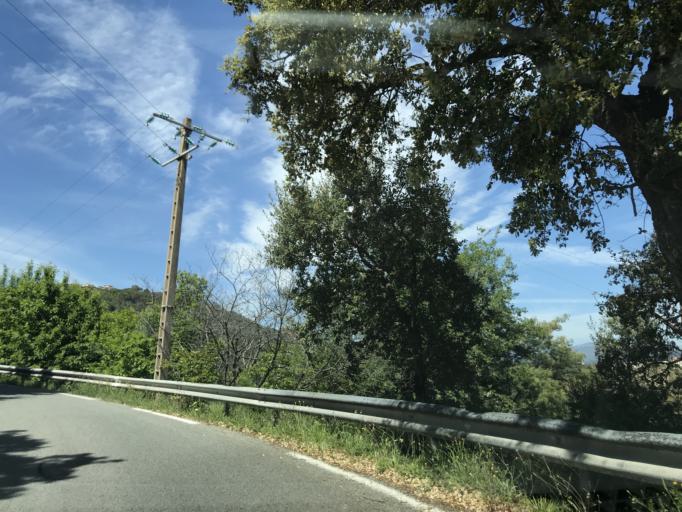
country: FR
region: Provence-Alpes-Cote d'Azur
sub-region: Departement du Var
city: Tanneron
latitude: 43.5857
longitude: 6.8926
